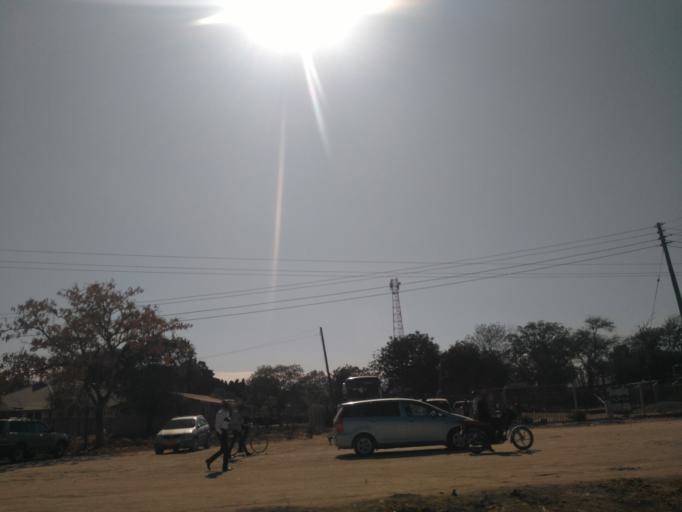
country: TZ
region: Dodoma
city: Dodoma
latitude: -6.1588
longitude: 35.7466
